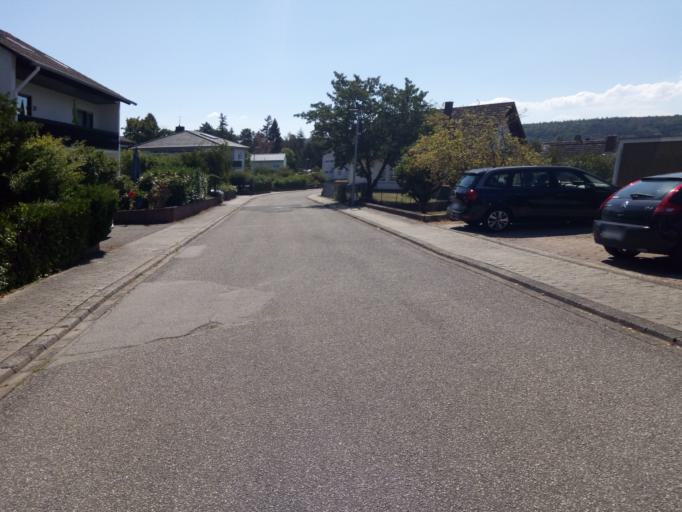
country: DE
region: Rheinland-Pfalz
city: Waldlaubersheim
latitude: 49.9288
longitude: 7.8371
